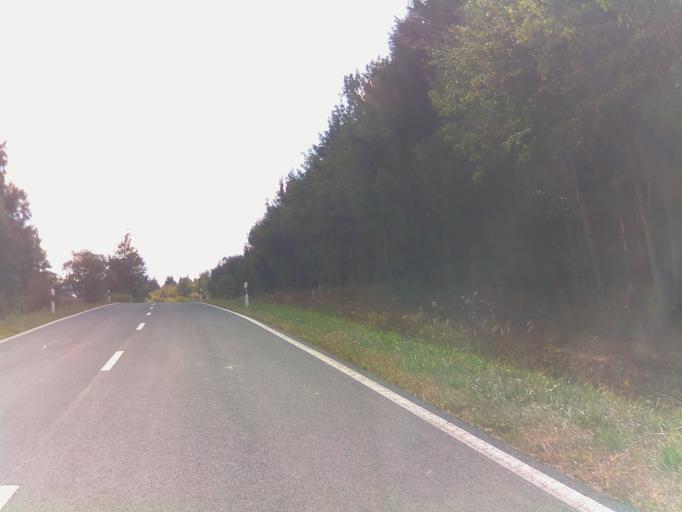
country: DE
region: Thuringia
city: Birx
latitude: 50.5163
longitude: 10.0576
